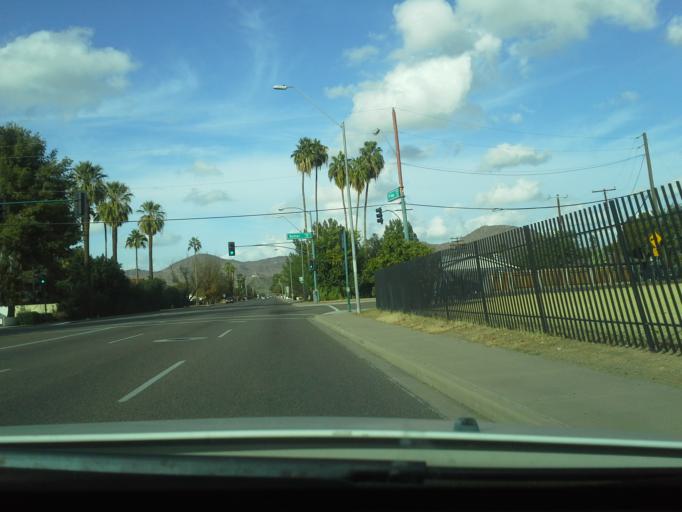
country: US
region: Arizona
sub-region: Maricopa County
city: Glendale
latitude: 33.5598
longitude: -112.0825
